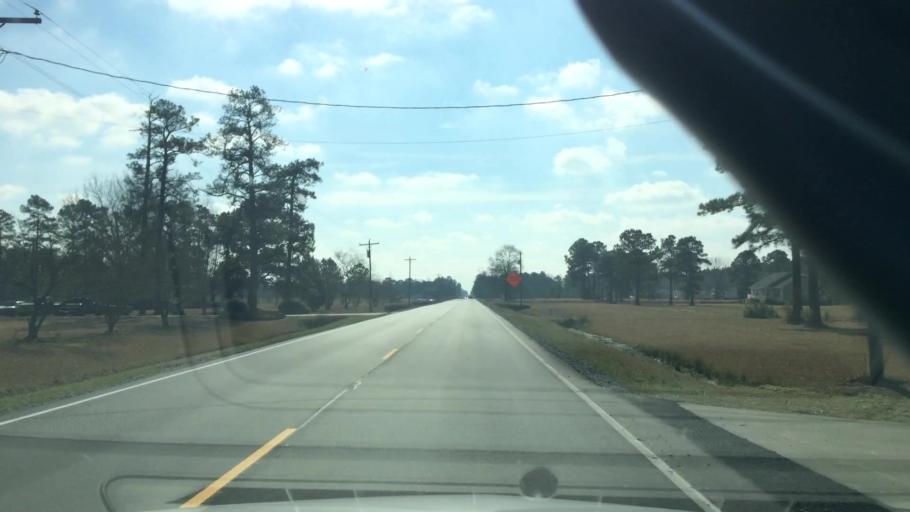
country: US
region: North Carolina
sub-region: Duplin County
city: Beulaville
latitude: 35.0225
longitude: -77.7498
